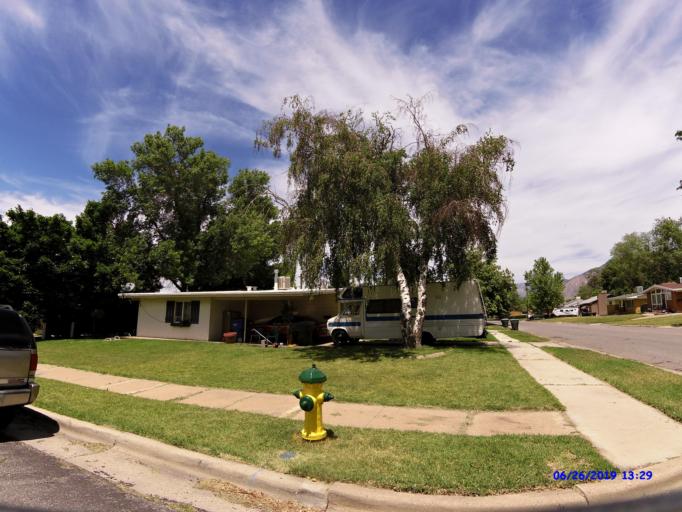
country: US
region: Utah
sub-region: Weber County
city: South Ogden
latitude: 41.2020
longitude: -111.9582
